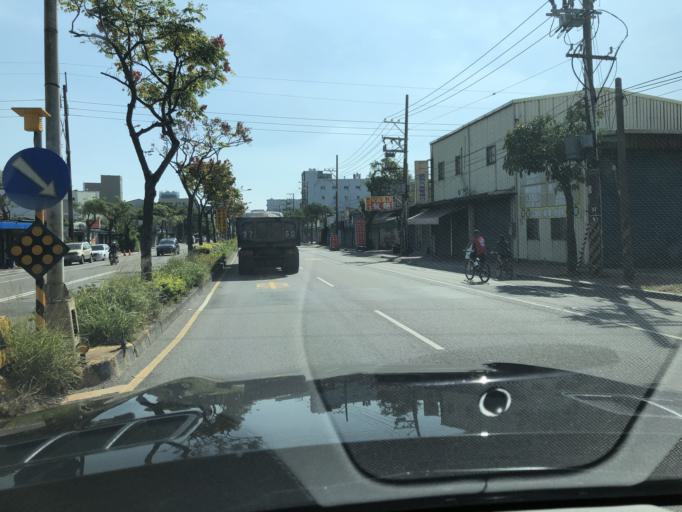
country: TW
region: Taiwan
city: Taoyuan City
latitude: 25.0757
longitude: 121.2853
